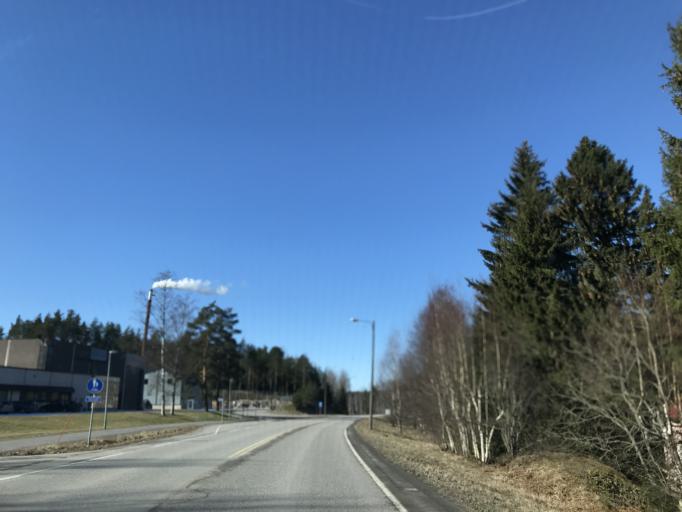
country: FI
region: Uusimaa
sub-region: Raaseporin
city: Pohja
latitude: 60.0997
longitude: 23.5361
